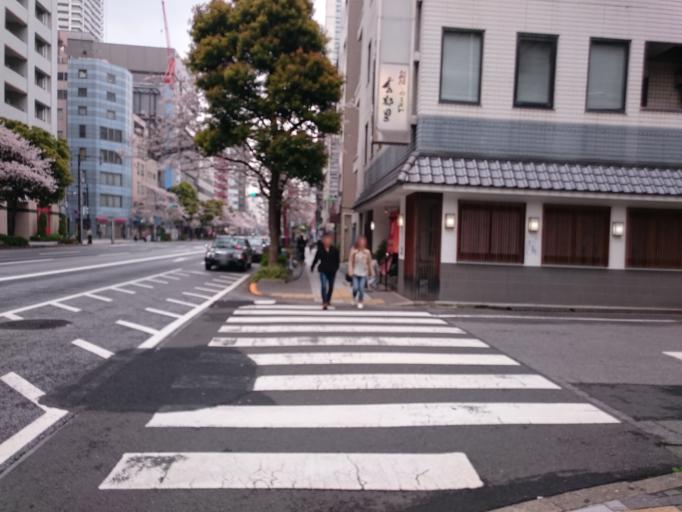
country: JP
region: Tokyo
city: Tokyo
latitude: 35.6823
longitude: 139.7859
